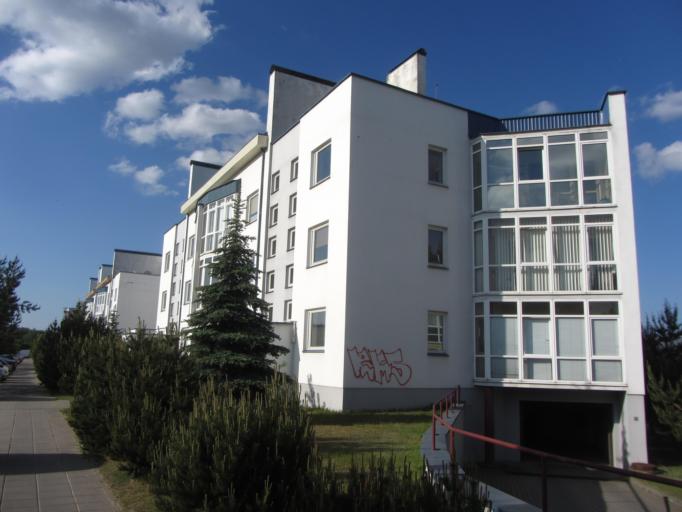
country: LT
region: Vilnius County
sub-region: Vilnius
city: Fabijoniskes
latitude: 54.7429
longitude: 25.2641
